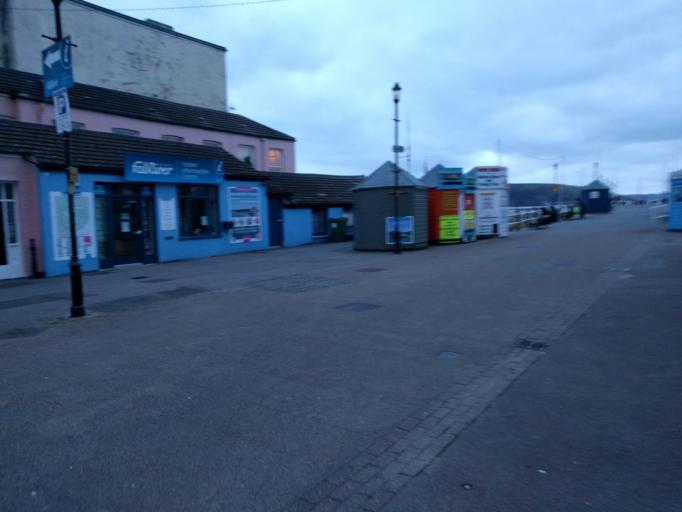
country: GB
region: England
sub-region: Cornwall
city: Falmouth
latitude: 50.1562
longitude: -5.0709
